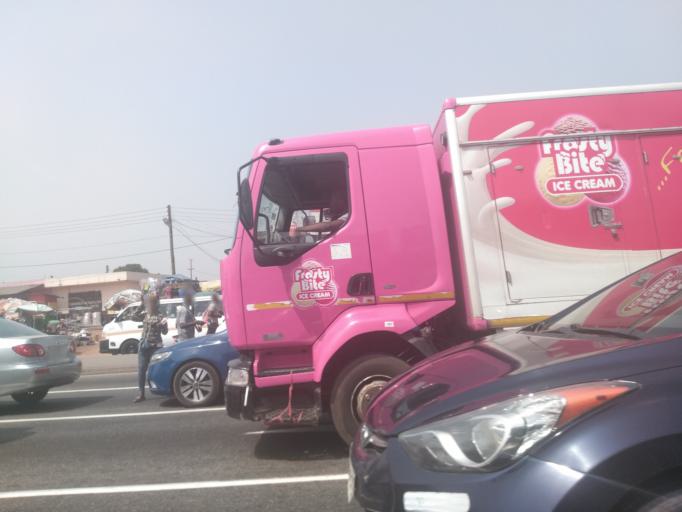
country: GH
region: Greater Accra
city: Dome
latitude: 5.6071
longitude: -0.2482
